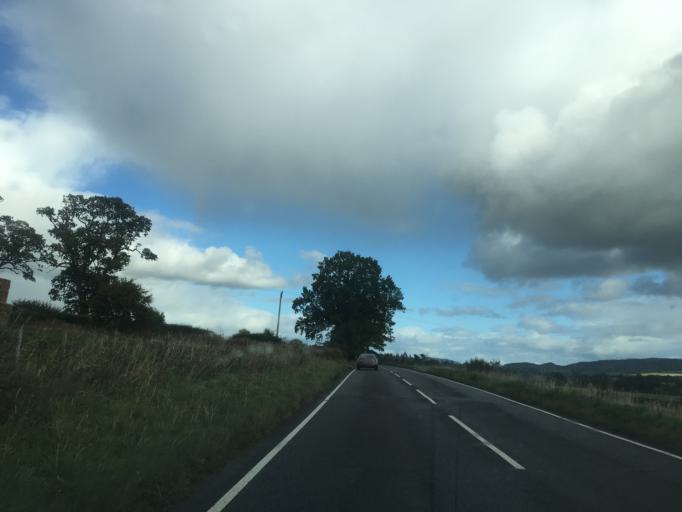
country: GB
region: Scotland
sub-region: Highland
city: Beauly
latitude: 57.4618
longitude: -4.4524
